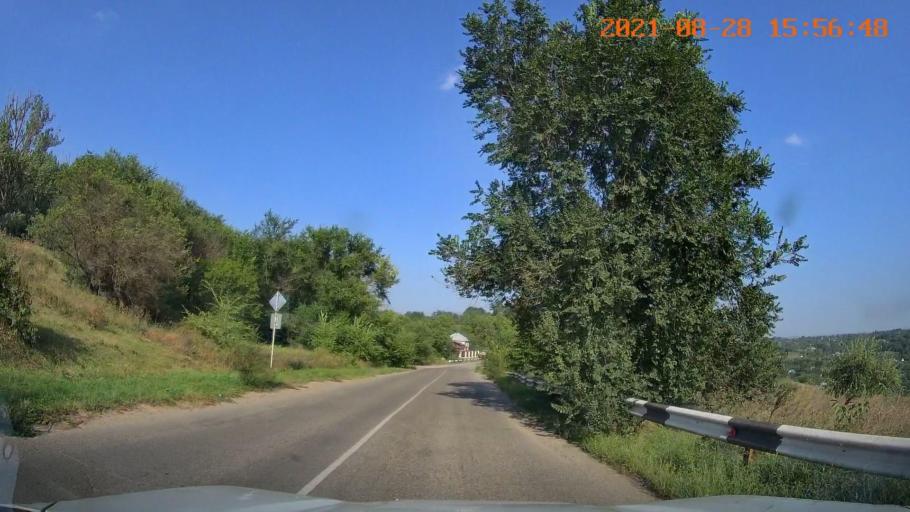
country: RU
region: Stavropol'skiy
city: Tatarka
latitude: 44.9608
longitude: 41.9341
